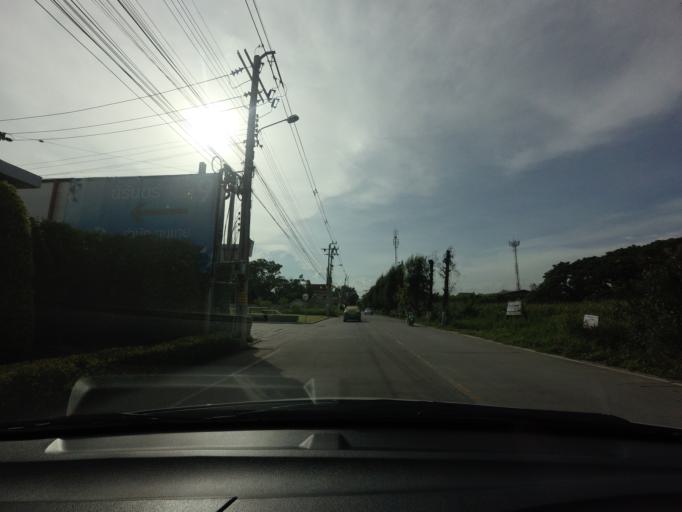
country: TH
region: Bangkok
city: Bang Na
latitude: 13.6499
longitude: 100.6576
